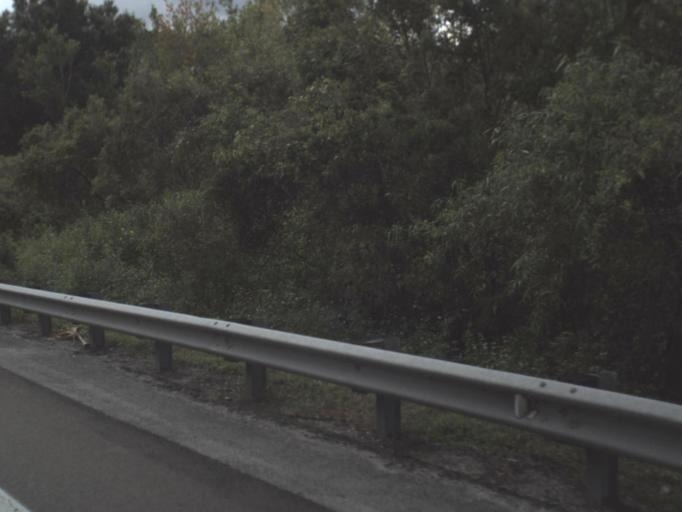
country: US
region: Florida
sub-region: Polk County
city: Highland City
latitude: 27.9983
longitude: -81.8552
